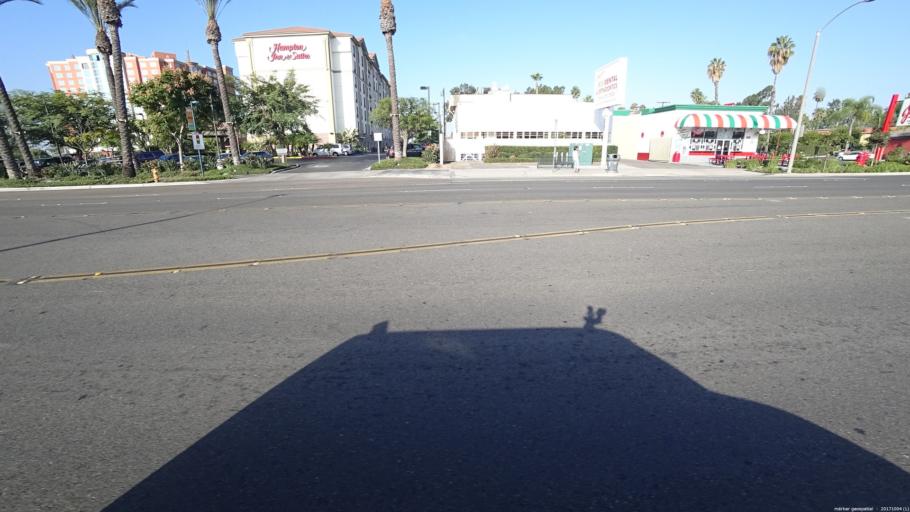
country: US
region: California
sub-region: Orange County
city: Garden Grove
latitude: 33.7924
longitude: -117.9149
